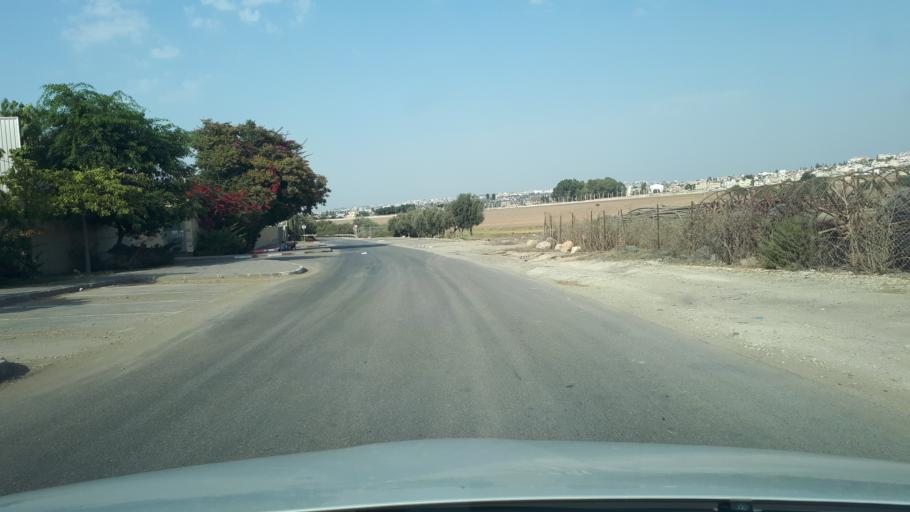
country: IL
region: Central District
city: Rosh Ha'Ayin
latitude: 32.0830
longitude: 34.9439
